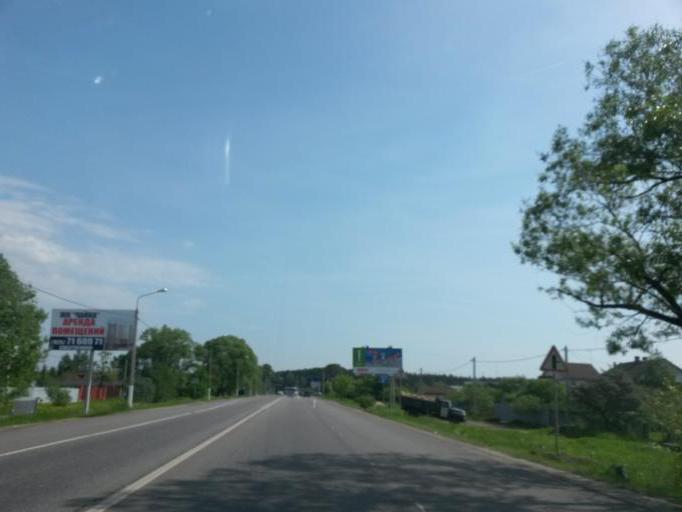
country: RU
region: Moskovskaya
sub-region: Chekhovskiy Rayon
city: Chekhov
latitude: 55.1864
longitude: 37.4975
